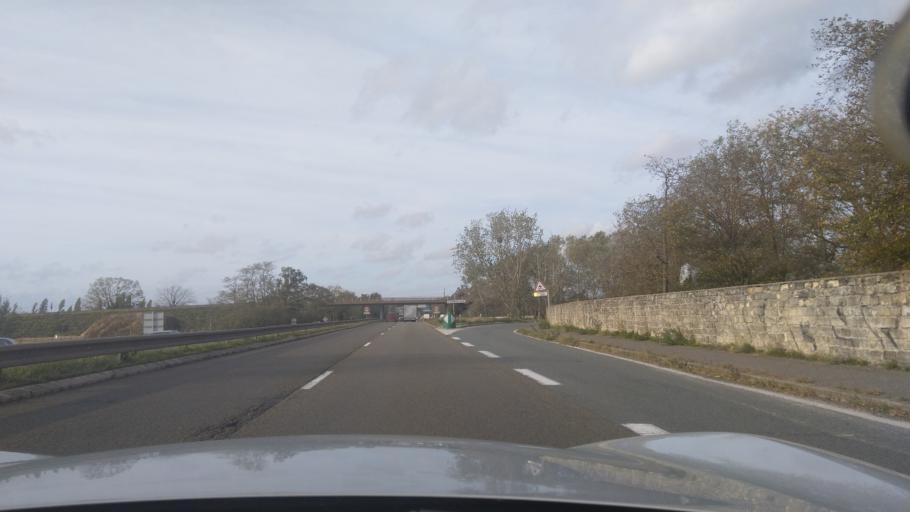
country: FR
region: Ile-de-France
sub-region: Departement des Yvelines
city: Conflans-Sainte-Honorine
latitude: 48.9789
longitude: 2.0876
